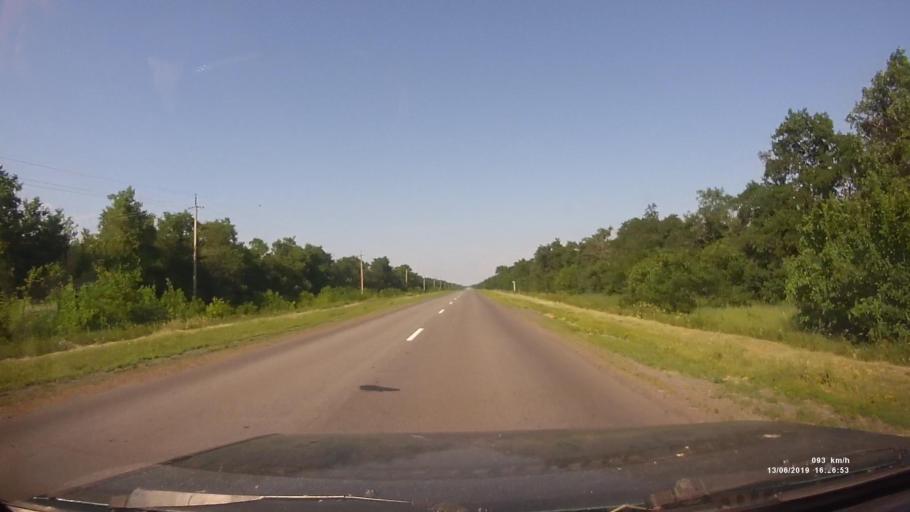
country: RU
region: Rostov
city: Kazanskaya
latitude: 49.8087
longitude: 41.1733
